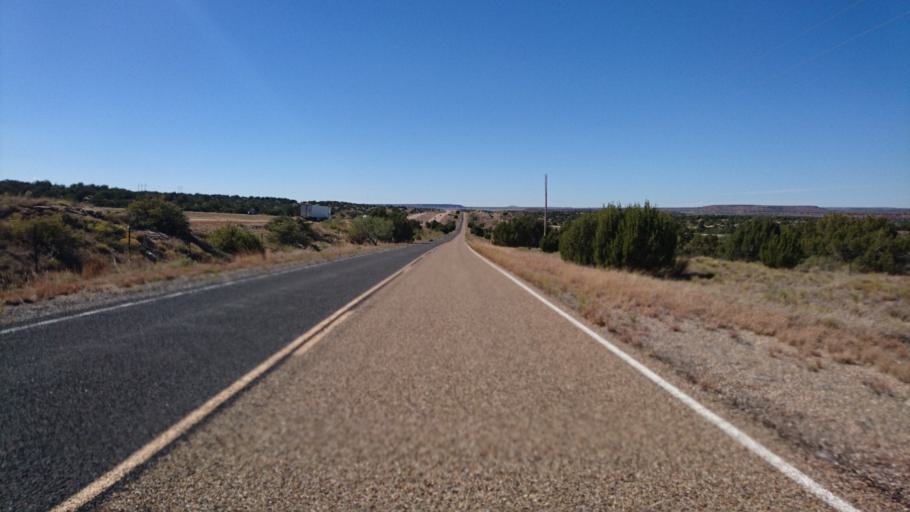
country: US
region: New Mexico
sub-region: Quay County
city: Tucumcari
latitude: 35.0670
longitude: -104.1892
